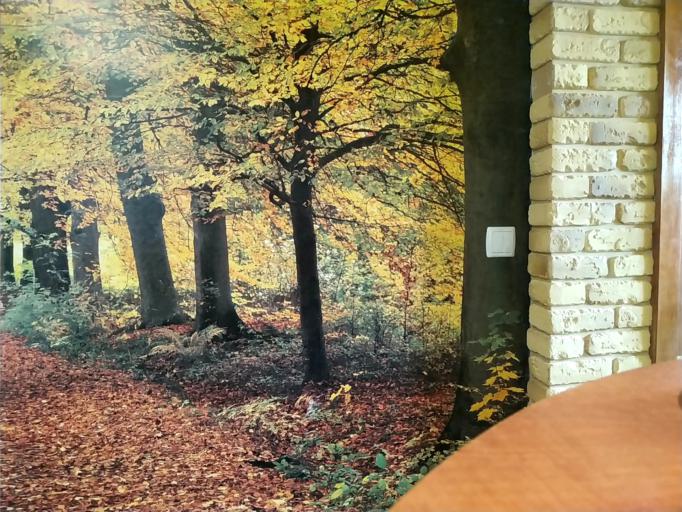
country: RU
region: Novgorod
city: Opechenskiy Posad
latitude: 58.2677
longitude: 34.0232
